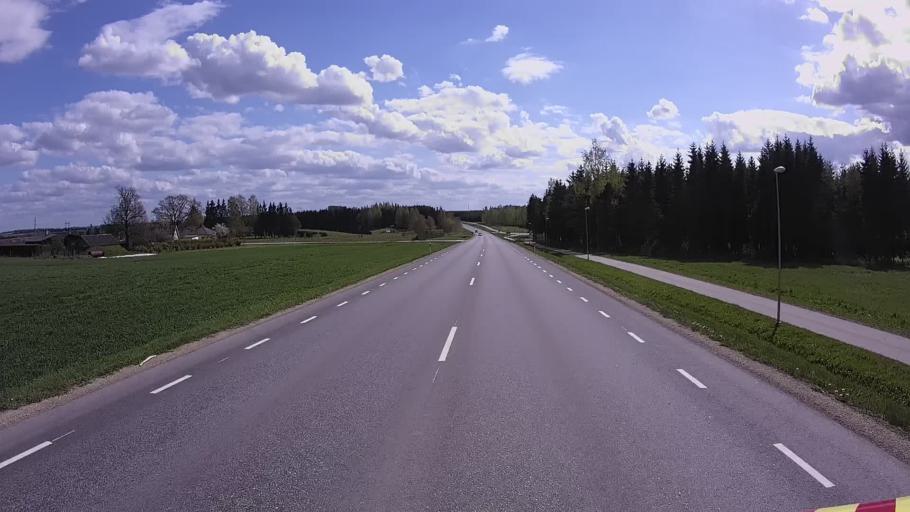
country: EE
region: Jogevamaa
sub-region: Tabivere vald
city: Tabivere
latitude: 58.4892
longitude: 26.6825
